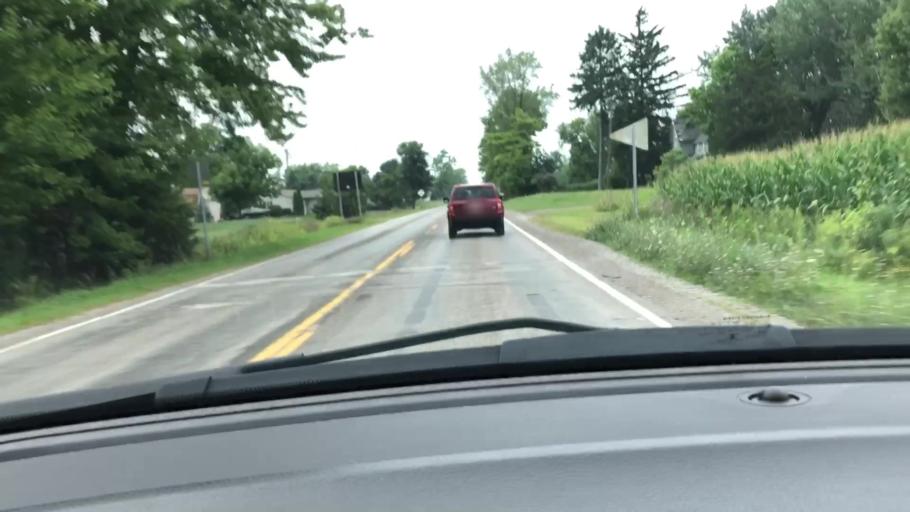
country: US
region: Michigan
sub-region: Saginaw County
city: Freeland
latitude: 43.5449
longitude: -84.0902
